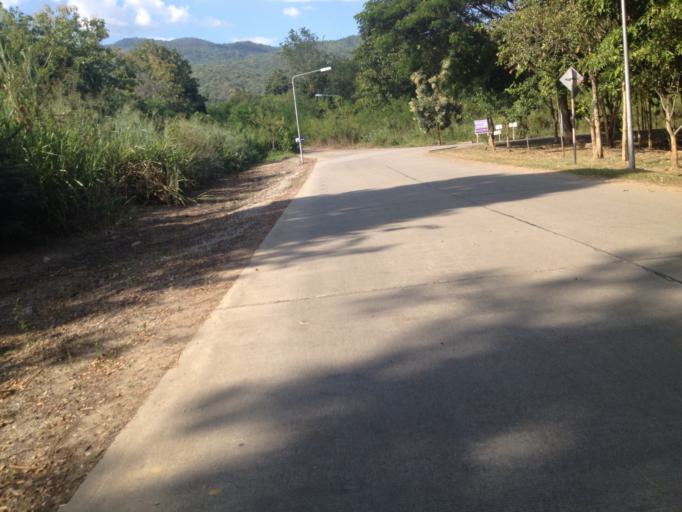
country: TH
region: Chiang Mai
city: Chiang Mai
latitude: 18.7624
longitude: 98.9358
